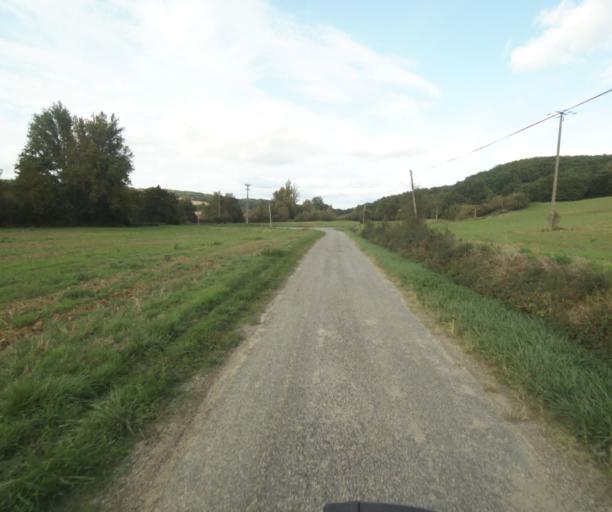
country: FR
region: Midi-Pyrenees
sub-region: Departement du Tarn-et-Garonne
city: Beaumont-de-Lomagne
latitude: 43.8204
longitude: 1.0899
